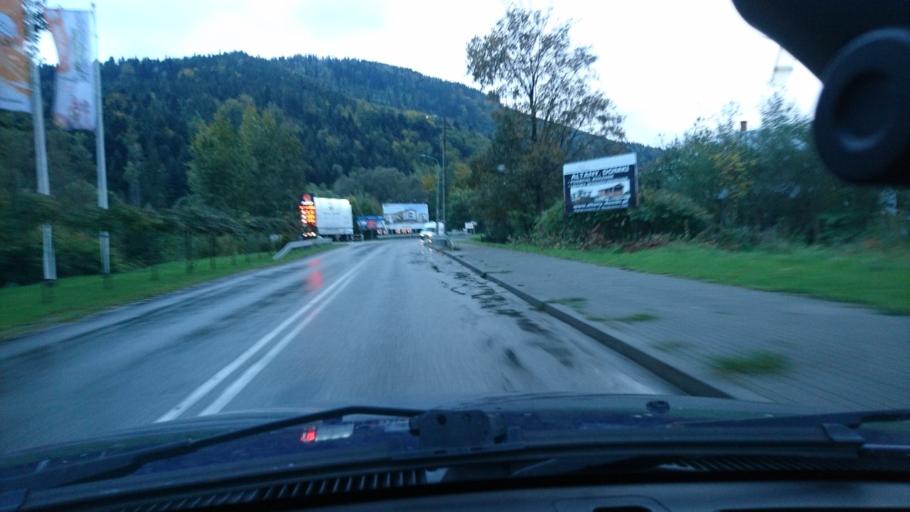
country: PL
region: Silesian Voivodeship
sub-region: Powiat bielski
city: Szczyrk
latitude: 49.7228
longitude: 19.0457
